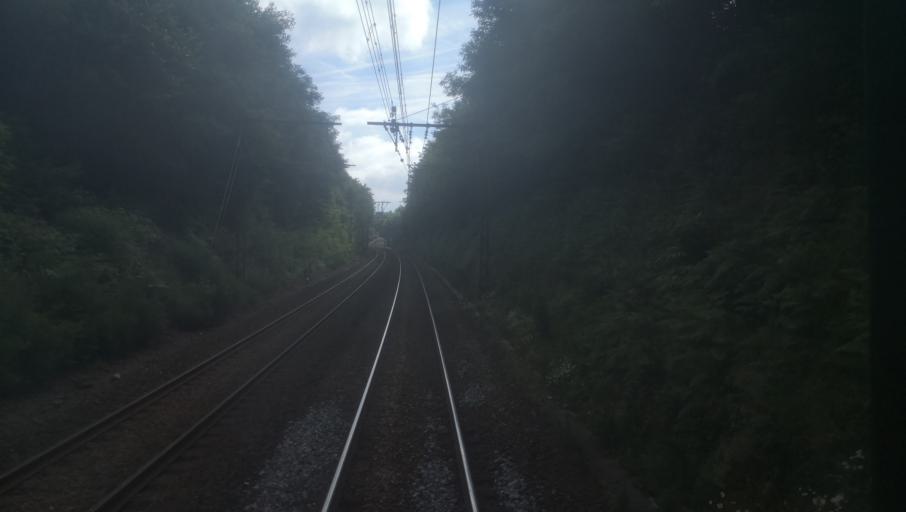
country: FR
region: Limousin
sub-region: Departement de la Haute-Vienne
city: Le Palais-sur-Vienne
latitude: 45.8834
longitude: 1.3393
